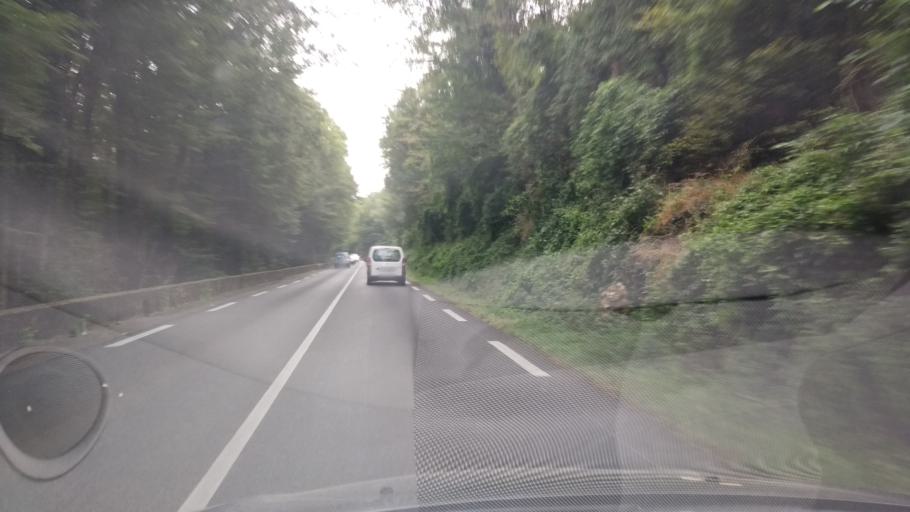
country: FR
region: Poitou-Charentes
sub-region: Departement de la Vienne
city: Saint-Benoit
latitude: 46.5481
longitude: 0.3512
